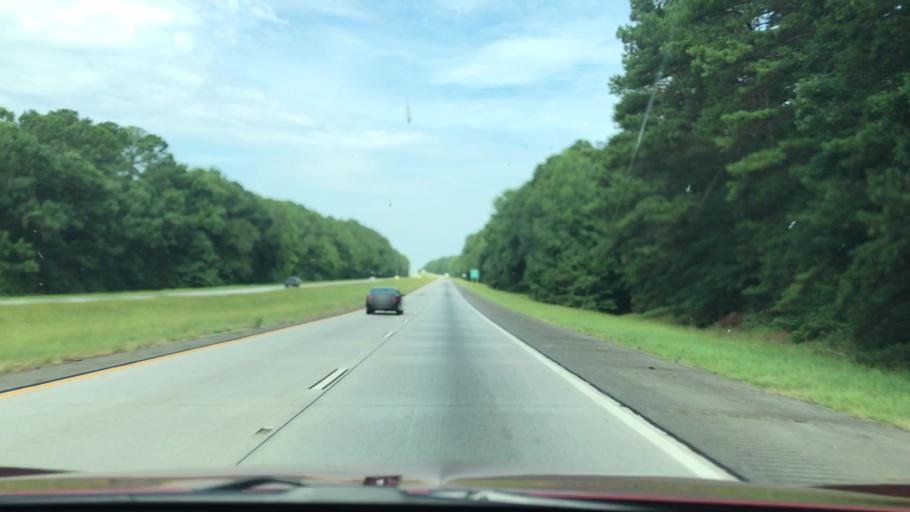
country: US
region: Georgia
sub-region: Warren County
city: Firing Range
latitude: 33.5007
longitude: -82.7847
